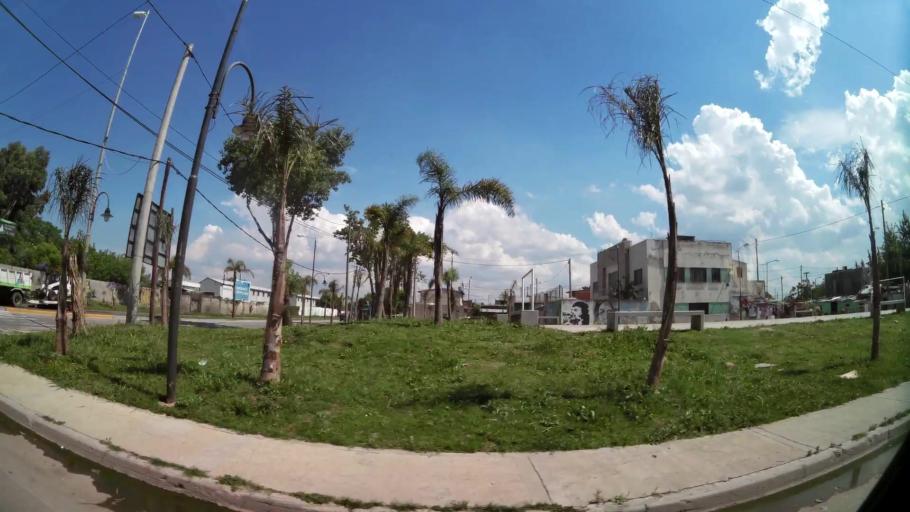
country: AR
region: Buenos Aires
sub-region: Partido de Tigre
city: Tigre
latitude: -34.4644
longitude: -58.5956
